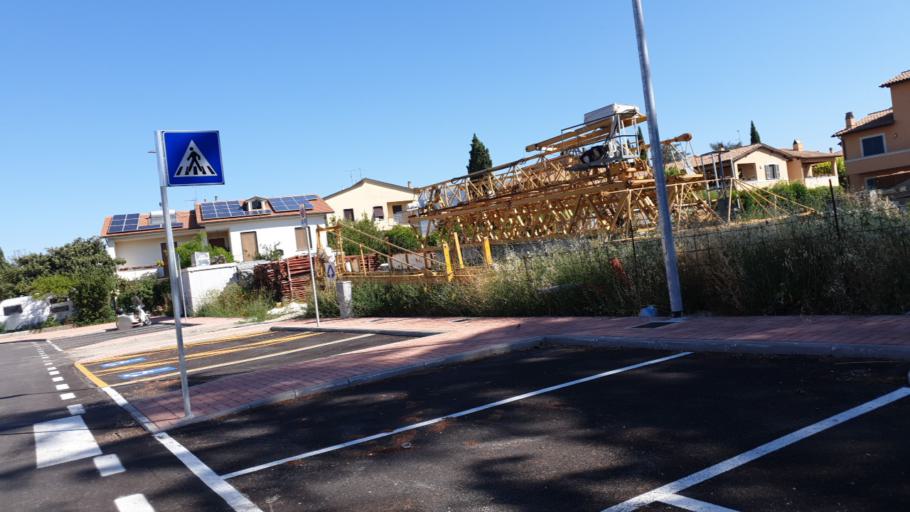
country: IT
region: Umbria
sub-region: Provincia di Perugia
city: Foligno
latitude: 42.9547
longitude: 12.6919
